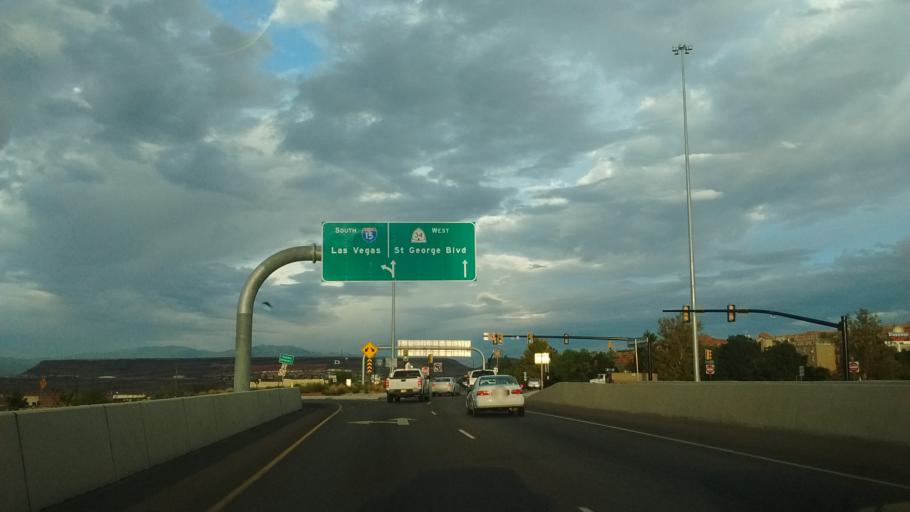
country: US
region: Utah
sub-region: Washington County
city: Saint George
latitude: 37.1097
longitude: -113.5582
